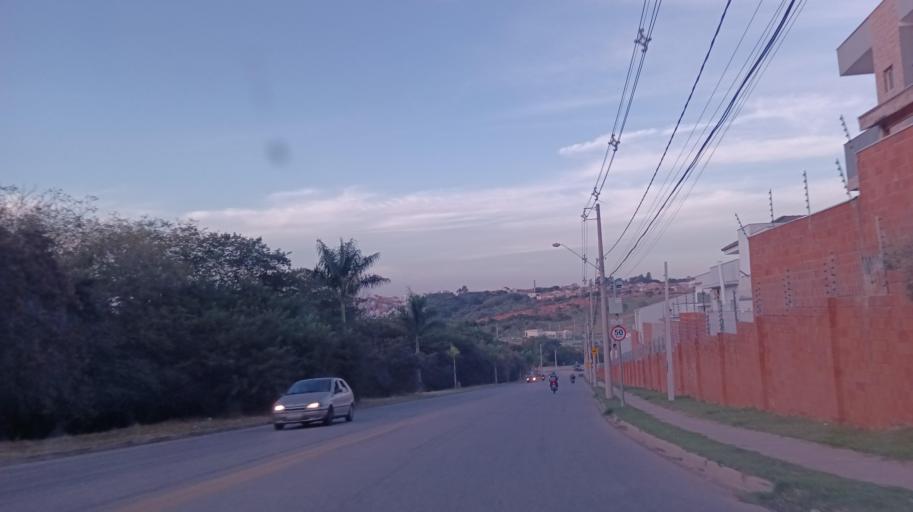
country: BR
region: Sao Paulo
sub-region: Sorocaba
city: Sorocaba
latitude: -23.4407
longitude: -47.4960
